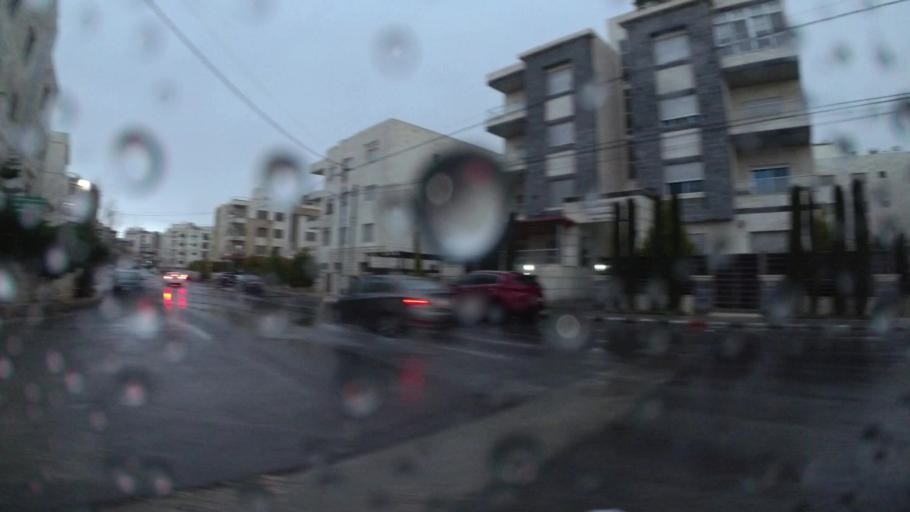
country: JO
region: Amman
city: Umm as Summaq
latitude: 31.9029
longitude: 35.8603
